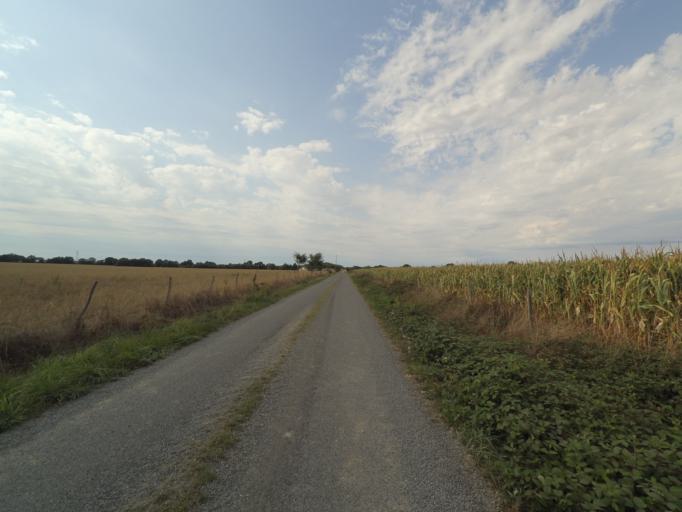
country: FR
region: Pays de la Loire
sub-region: Departement de la Loire-Atlantique
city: La Planche
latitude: 46.9923
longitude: -1.3982
